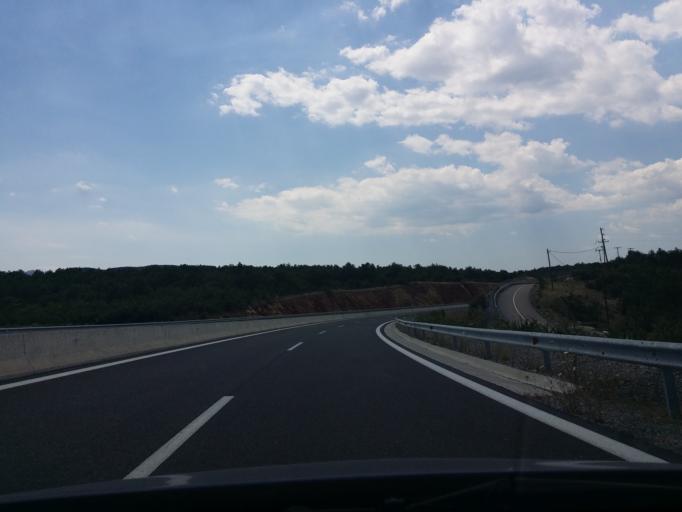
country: GR
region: Peloponnese
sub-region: Nomos Arkadias
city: Megalopoli
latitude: 37.3038
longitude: 22.2017
